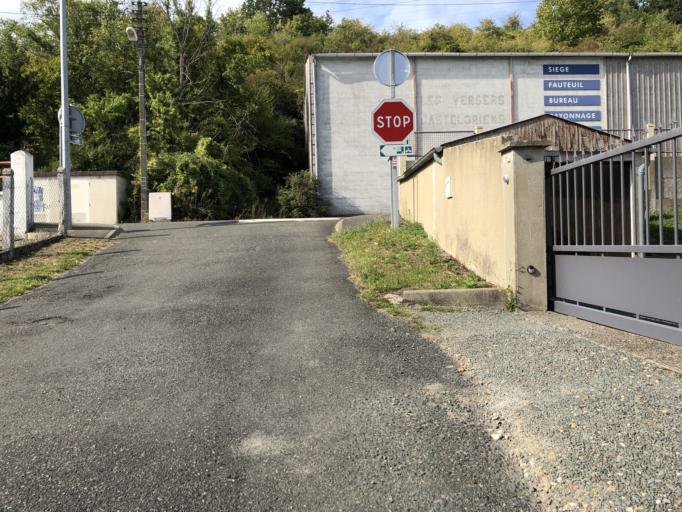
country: FR
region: Pays de la Loire
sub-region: Departement de la Sarthe
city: Chateau-du-Loir
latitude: 47.6824
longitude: 0.4288
